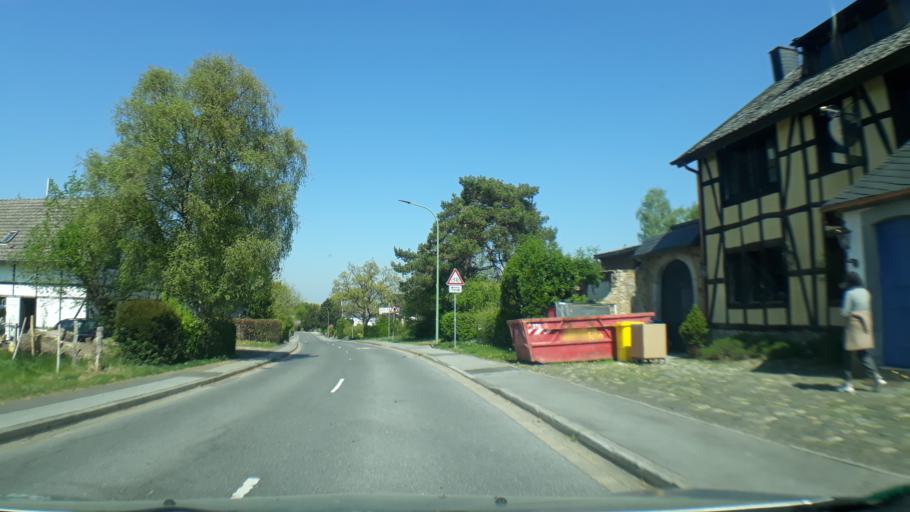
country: DE
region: North Rhine-Westphalia
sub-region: Regierungsbezirk Koln
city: Roetgen
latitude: 50.6390
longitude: 6.2023
